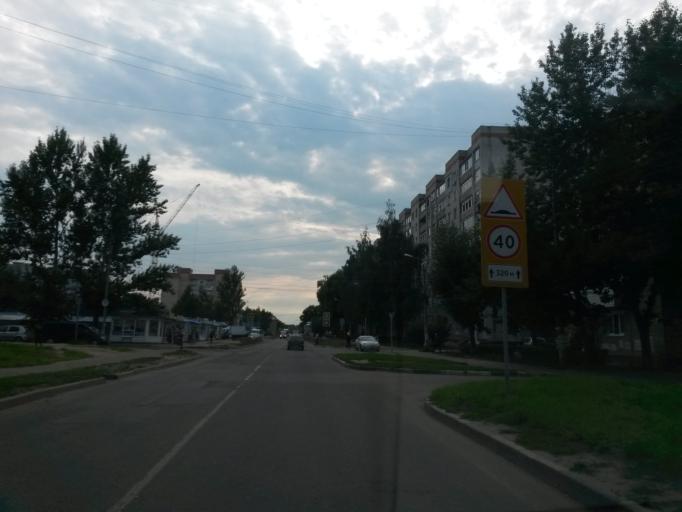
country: RU
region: Jaroslavl
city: Yaroslavl
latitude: 57.6072
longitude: 39.8223
